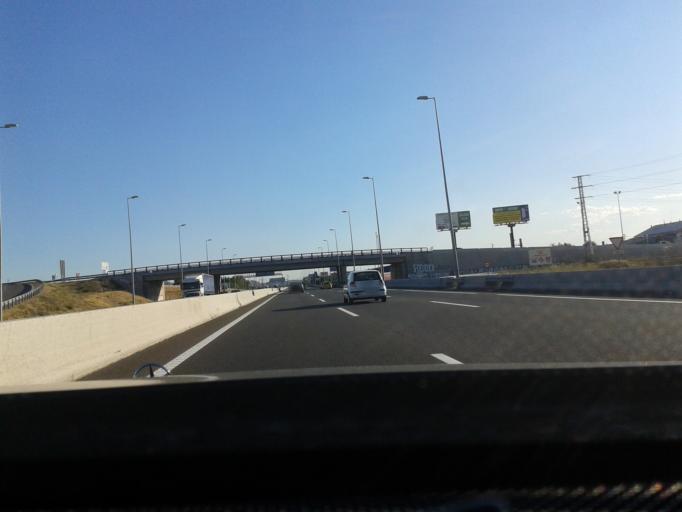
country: ES
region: Castille-La Mancha
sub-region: Provincia de Guadalajara
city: Azuqueca de Henares
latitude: 40.5557
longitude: -3.2623
